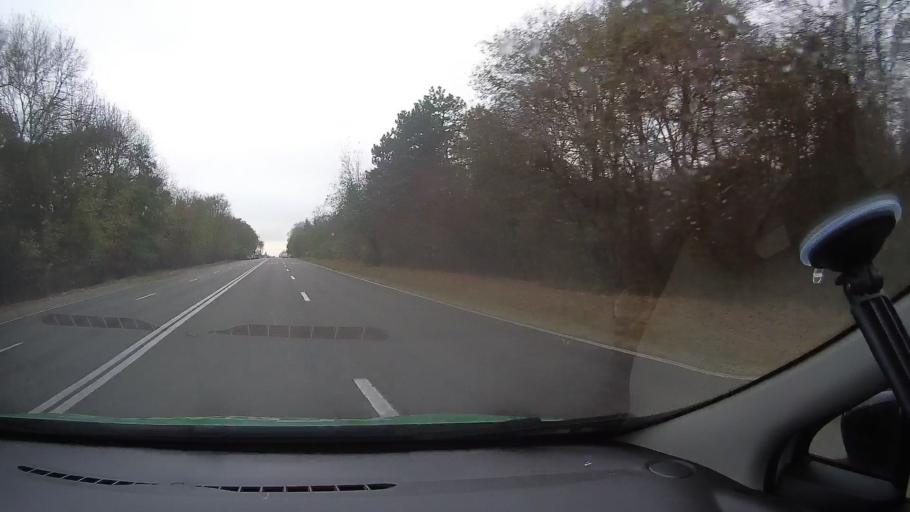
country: RO
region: Constanta
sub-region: Comuna Valu lui Traian
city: Valu lui Traian
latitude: 44.1651
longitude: 28.4940
